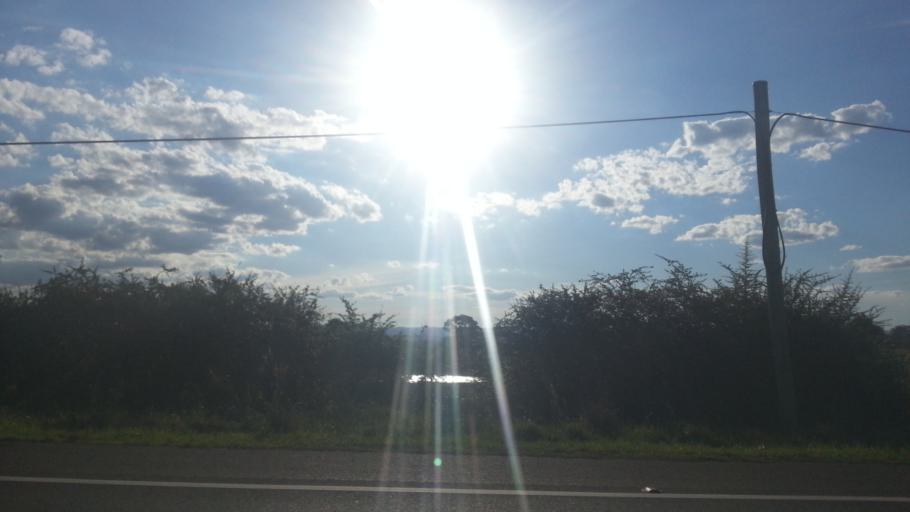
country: AU
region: New South Wales
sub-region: Liverpool
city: Luddenham
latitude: -33.8878
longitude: 150.6989
